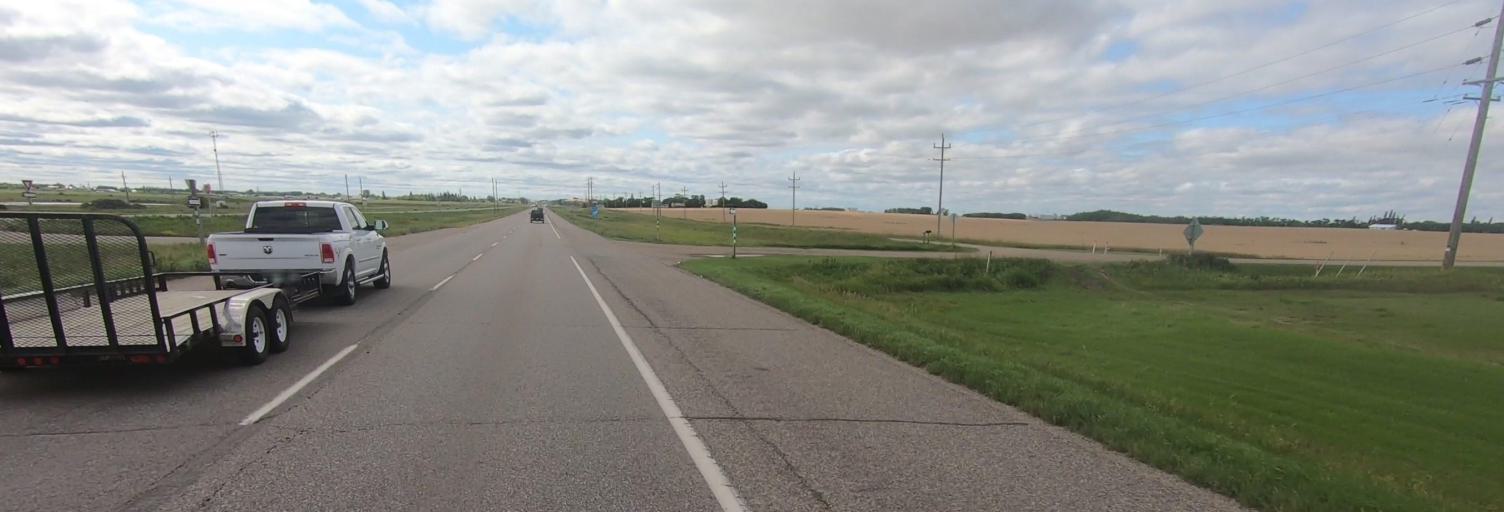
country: CA
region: Manitoba
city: Brandon
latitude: 49.8871
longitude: -99.9122
